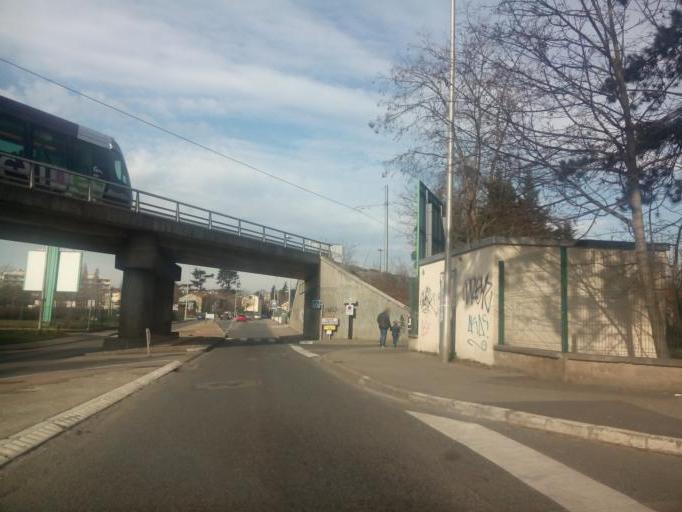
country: FR
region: Rhone-Alpes
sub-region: Departement du Rhone
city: Francheville
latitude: 45.7508
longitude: 4.7720
